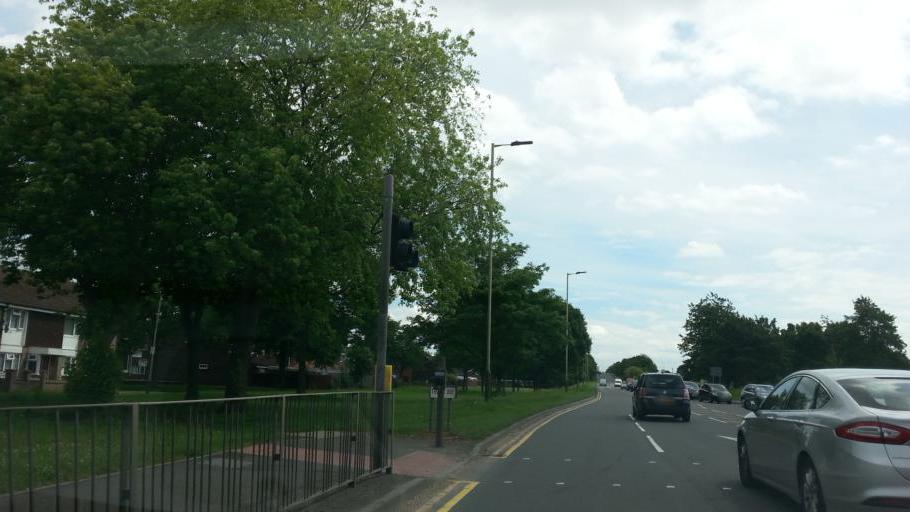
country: GB
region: England
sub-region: Leicestershire
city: Syston
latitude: 52.6656
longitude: -1.1006
